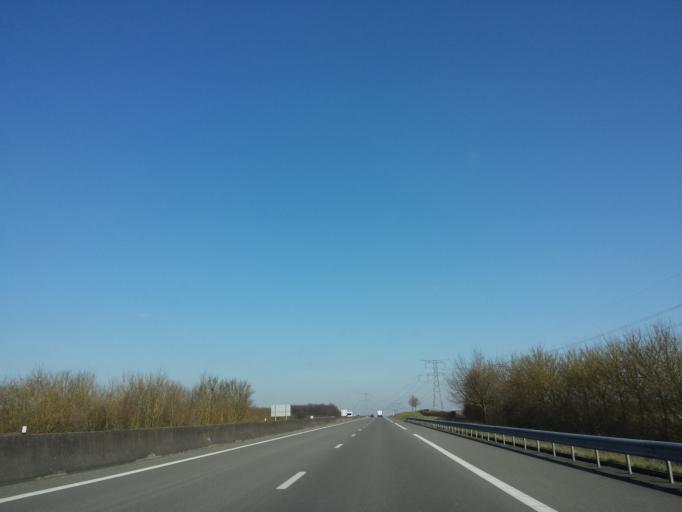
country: FR
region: Picardie
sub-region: Departement de la Somme
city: Saleux
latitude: 49.7754
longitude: 2.2353
